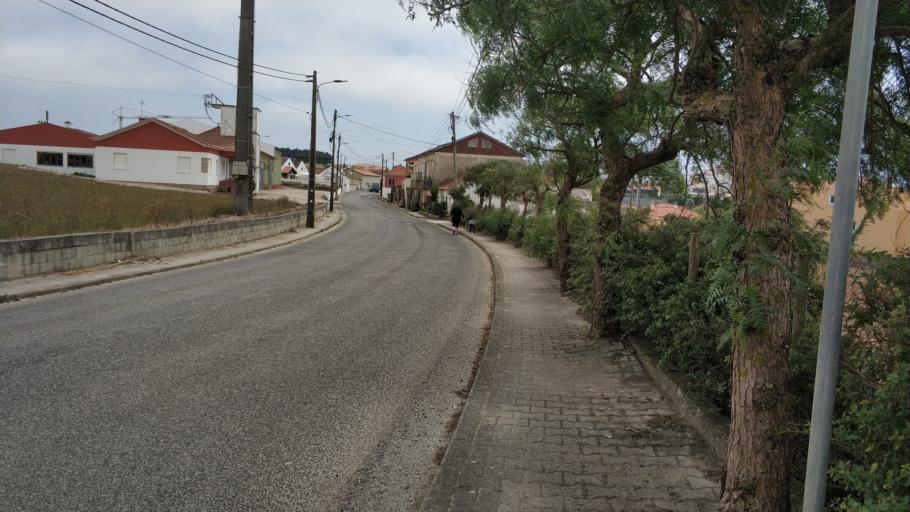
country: PT
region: Lisbon
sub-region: Lourinha
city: Lourinha
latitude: 39.2106
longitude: -9.3180
